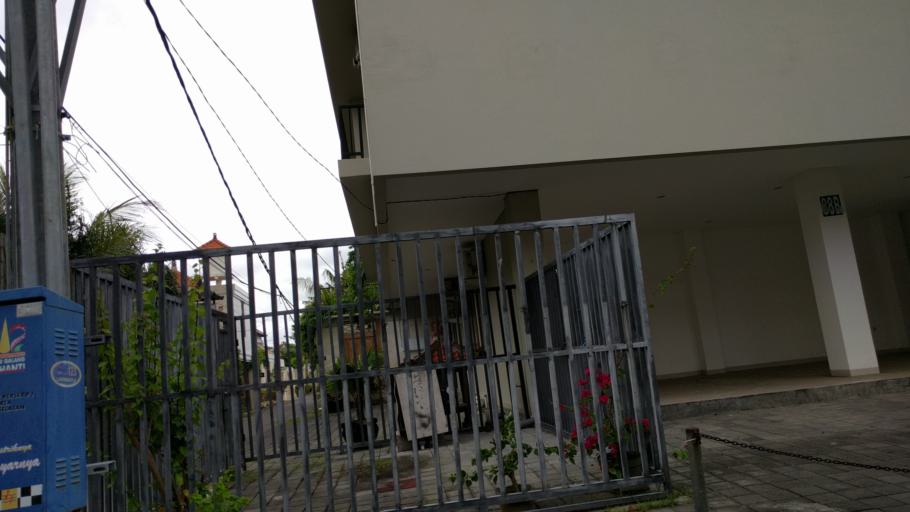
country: ID
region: Bali
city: Kuta
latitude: -8.6754
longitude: 115.1517
